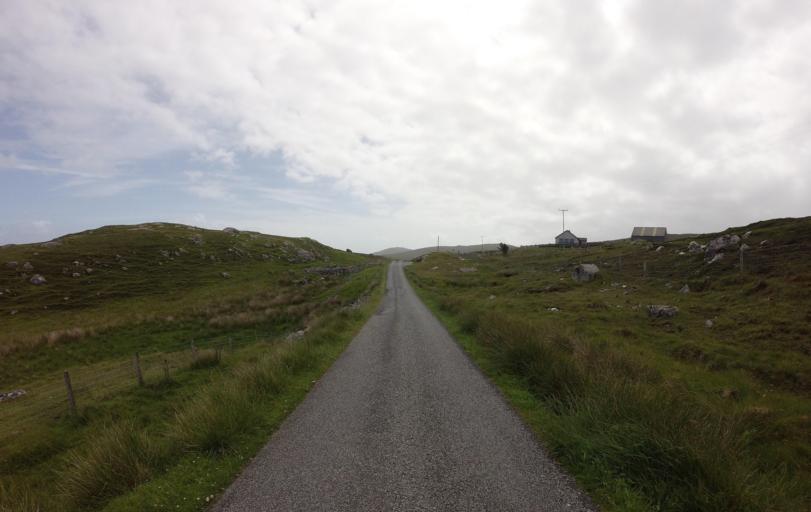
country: GB
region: Scotland
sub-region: Eilean Siar
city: Isle of South Uist
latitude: 57.1368
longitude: -7.3226
